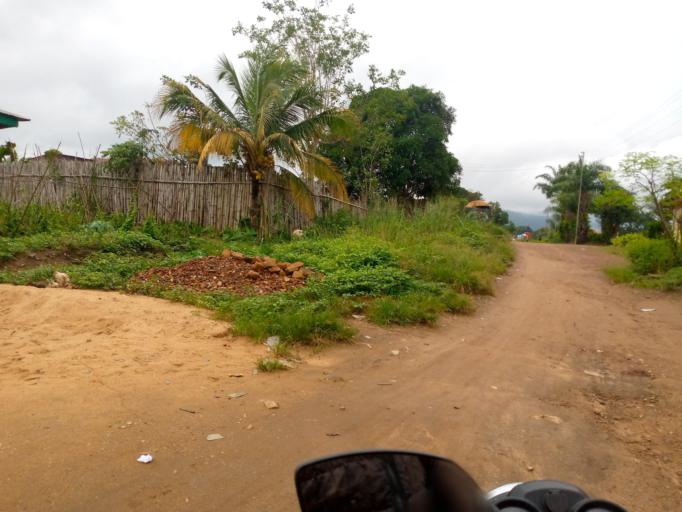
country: SL
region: Eastern Province
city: Kenema
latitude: 7.8418
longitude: -11.2023
